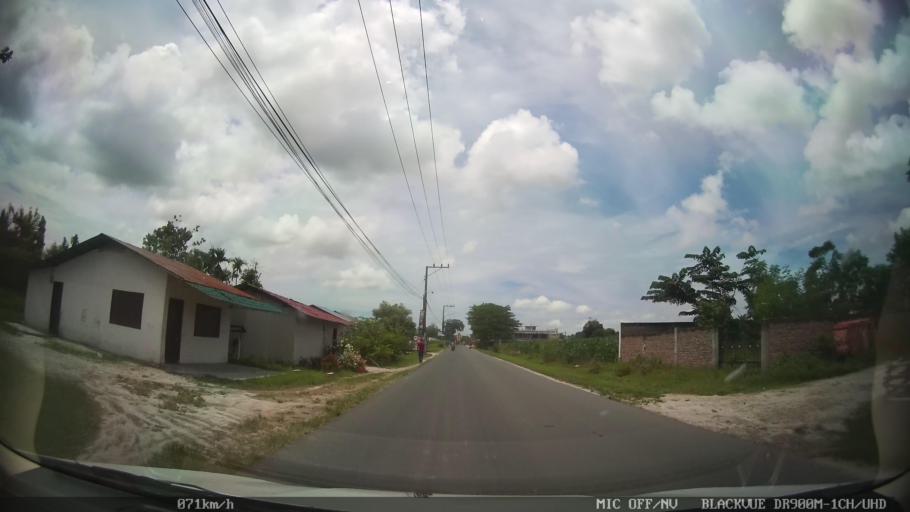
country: ID
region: North Sumatra
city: Percut
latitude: 3.5854
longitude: 98.8831
